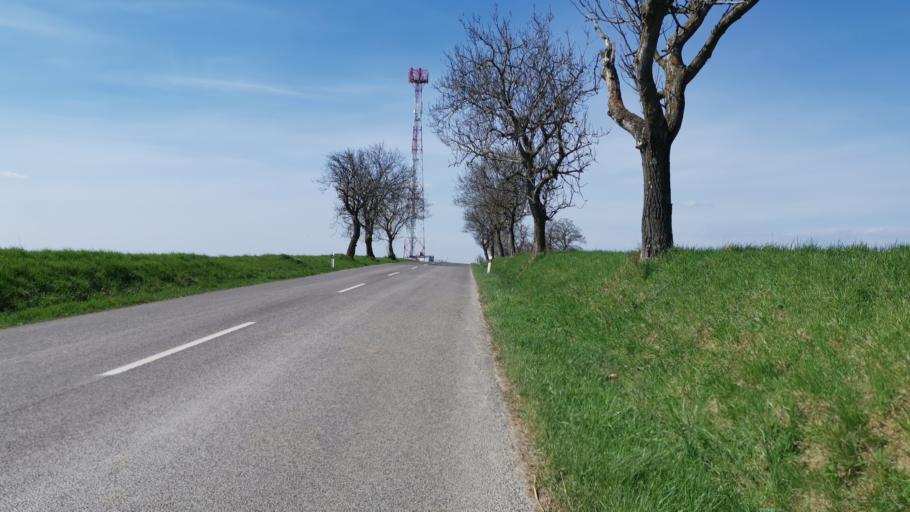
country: SK
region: Trnavsky
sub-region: Okres Skalica
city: Holic
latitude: 48.7416
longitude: 17.2039
